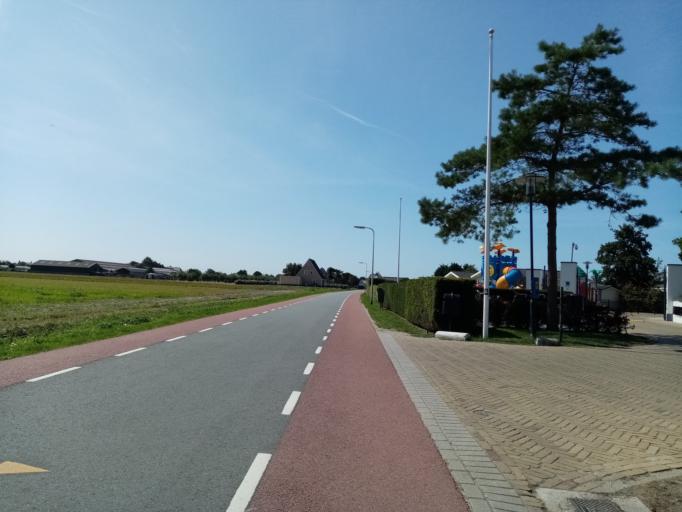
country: NL
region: South Holland
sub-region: Gemeente Noordwijkerhout
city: Noordwijkerhout
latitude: 52.2702
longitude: 4.4755
